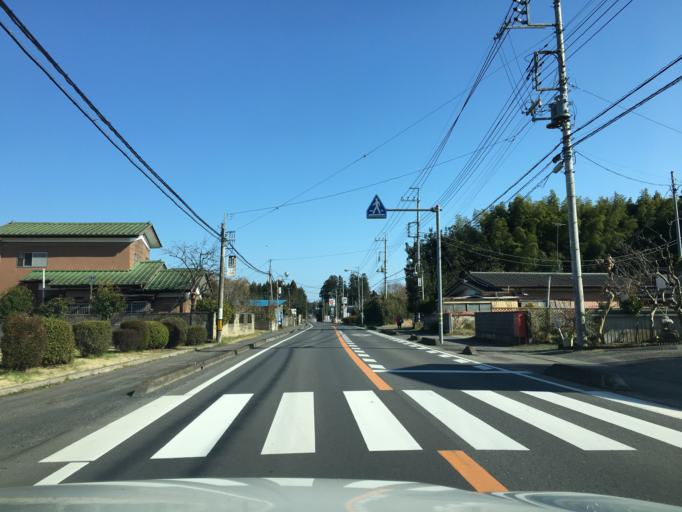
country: JP
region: Ibaraki
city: Omiya
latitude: 36.4733
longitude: 140.3887
